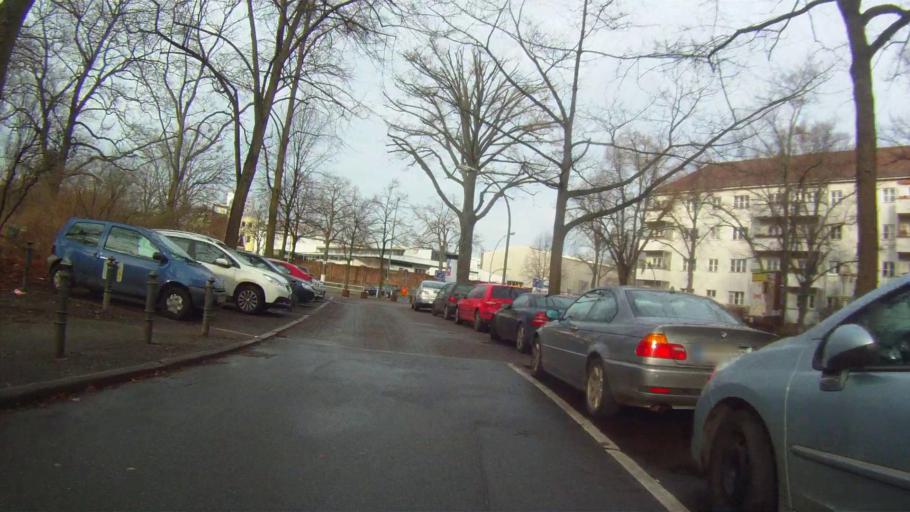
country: DE
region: Berlin
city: Schoneberg Bezirk
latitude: 52.4603
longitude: 13.3704
